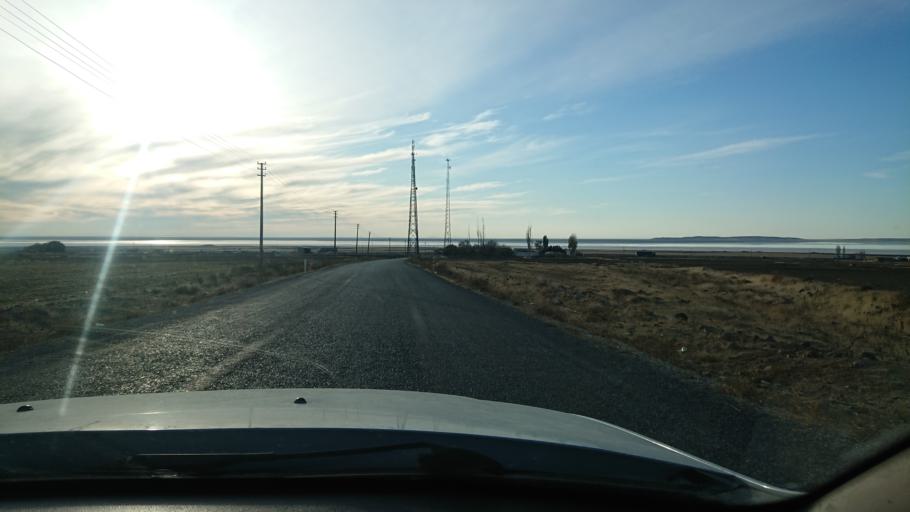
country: TR
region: Ankara
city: Sereflikochisar
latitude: 38.7426
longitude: 33.6705
